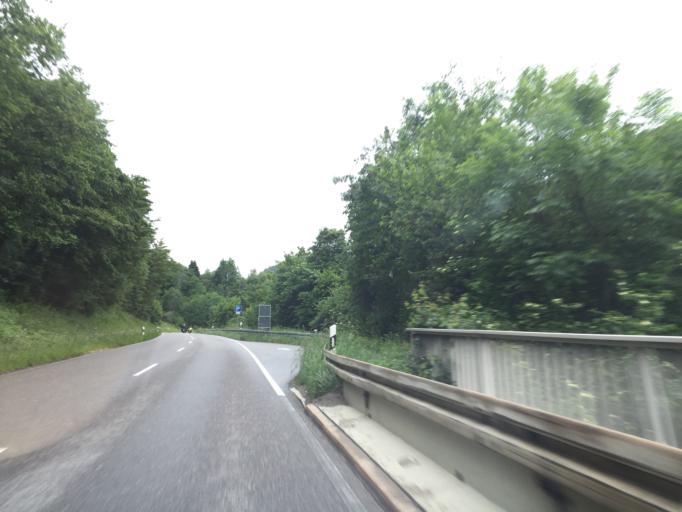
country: DE
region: Baden-Wuerttemberg
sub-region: Freiburg Region
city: Todtnau
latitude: 47.8298
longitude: 7.9404
